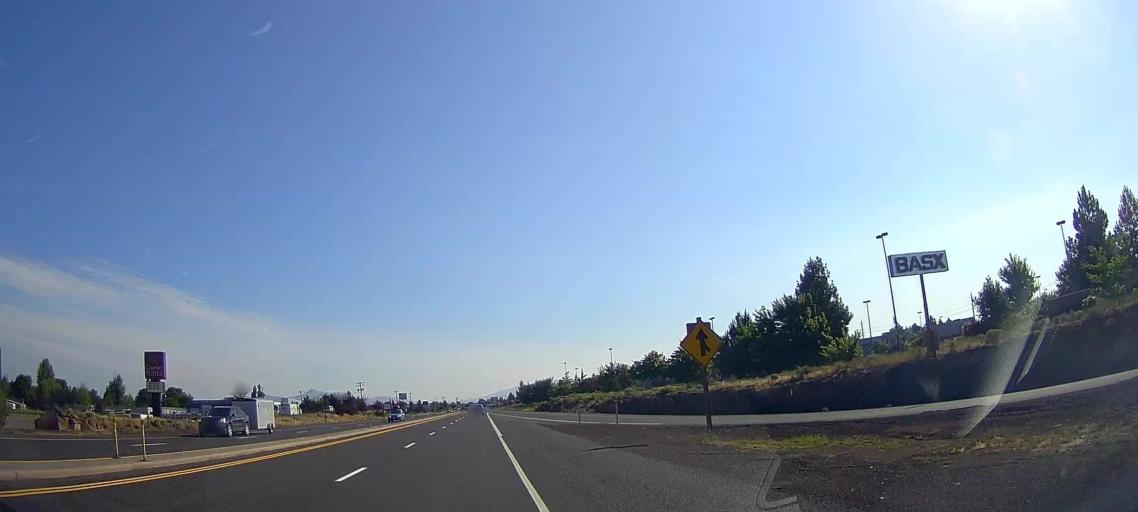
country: US
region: Oregon
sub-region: Deschutes County
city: Redmond
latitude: 44.2432
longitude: -121.1919
